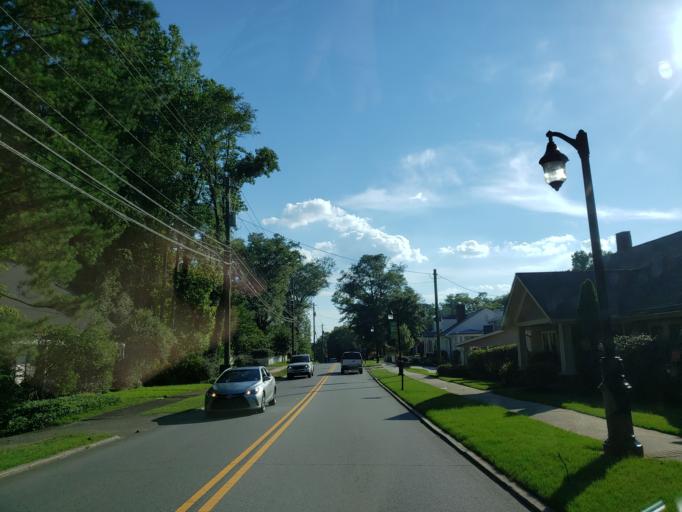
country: US
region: Georgia
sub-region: Cherokee County
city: Canton
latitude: 34.2365
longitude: -84.4821
